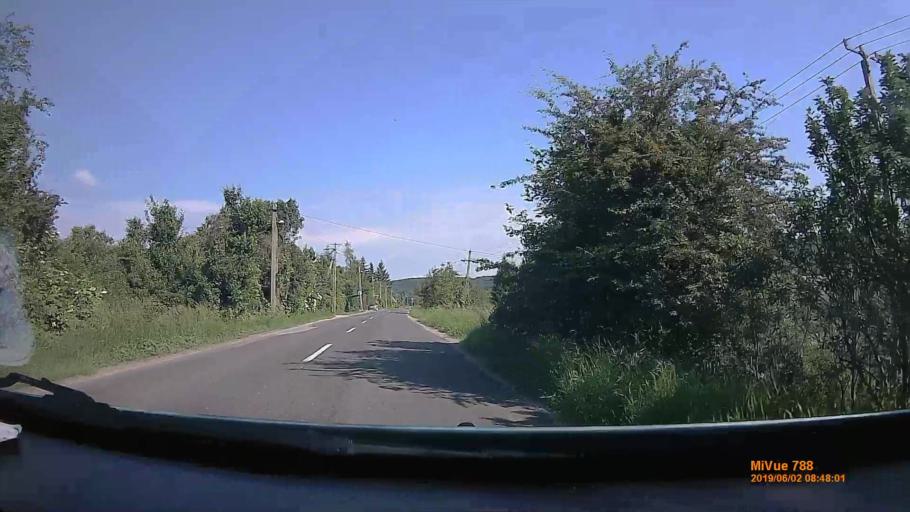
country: HU
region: Borsod-Abauj-Zemplen
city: Sajobabony
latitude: 48.1323
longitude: 20.7072
